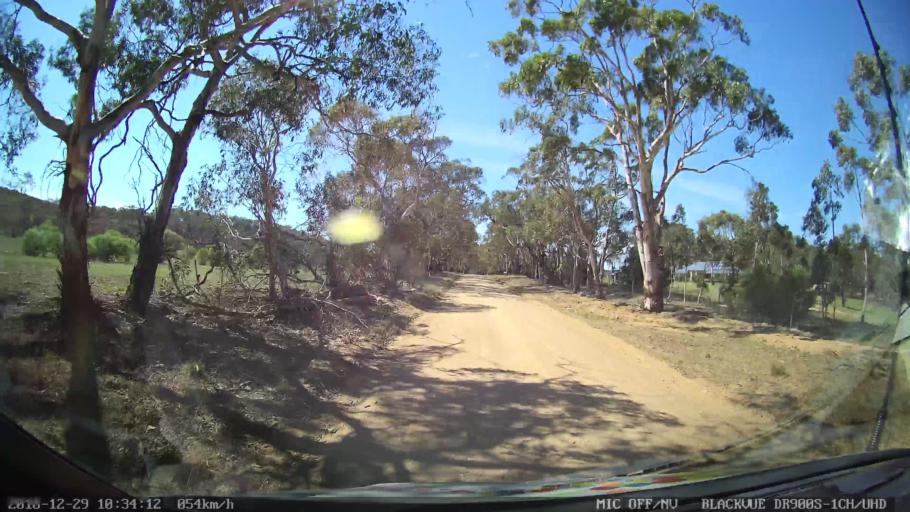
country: AU
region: New South Wales
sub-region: Yass Valley
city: Gundaroo
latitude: -34.9850
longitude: 149.4768
